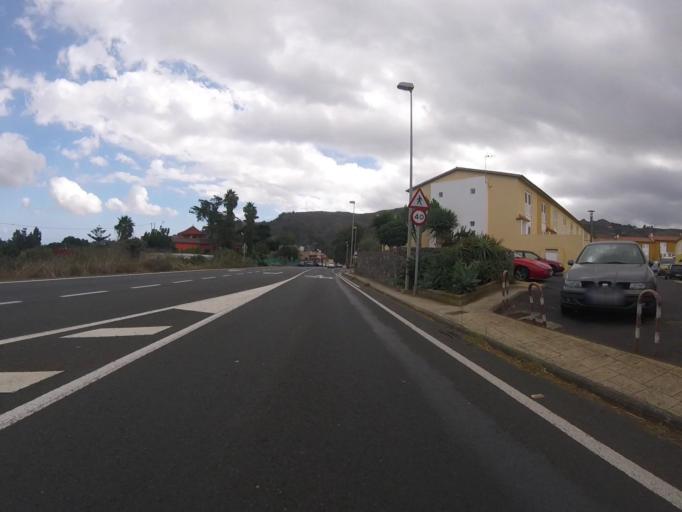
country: ES
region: Canary Islands
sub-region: Provincia de Las Palmas
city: Santa Brigida
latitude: 28.0276
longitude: -15.5063
